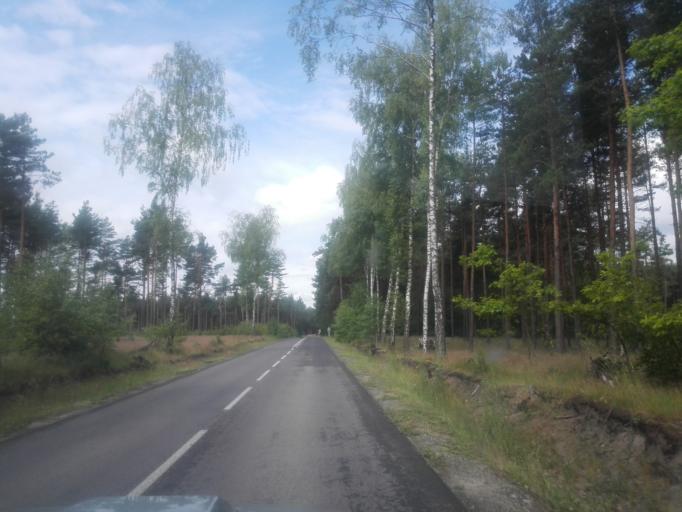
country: PL
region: Silesian Voivodeship
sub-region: Powiat myszkowski
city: Zarki
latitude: 50.7075
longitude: 19.3433
